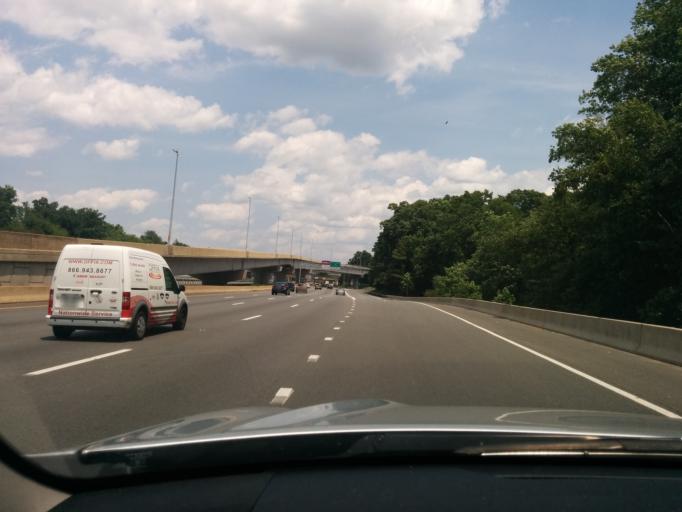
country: US
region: Virginia
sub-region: Fairfax County
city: Tysons Corner
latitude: 38.9321
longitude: -77.2531
